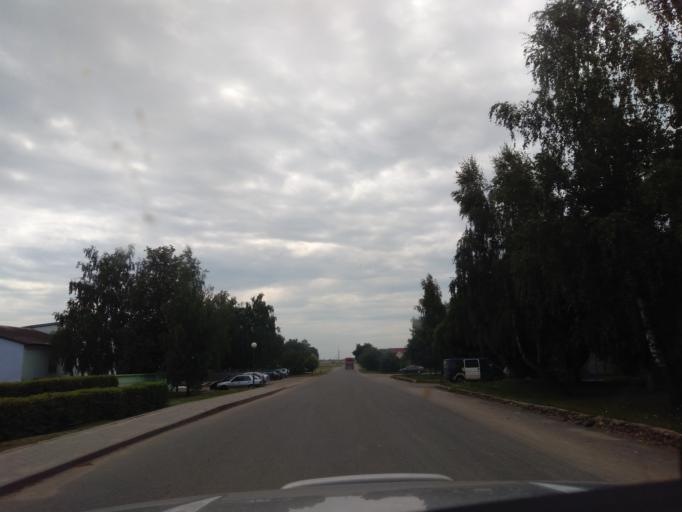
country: BY
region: Minsk
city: Kapyl'
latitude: 53.1398
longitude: 27.0955
